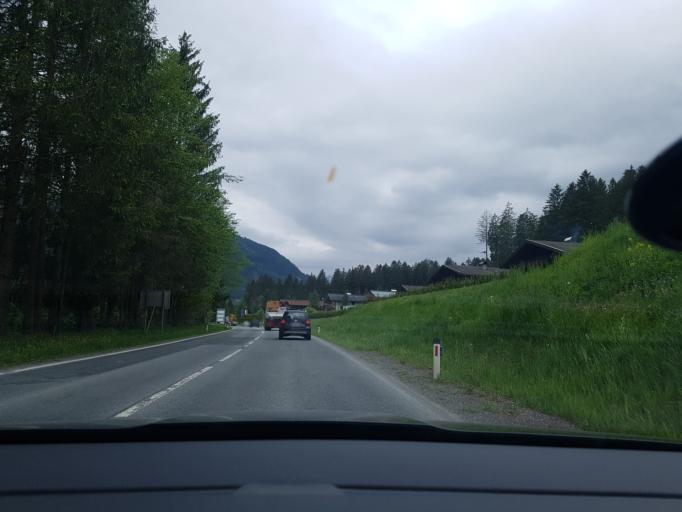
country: AT
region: Salzburg
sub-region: Politischer Bezirk Zell am See
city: Neukirchen am Grossvenediger
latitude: 47.2479
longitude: 12.2694
